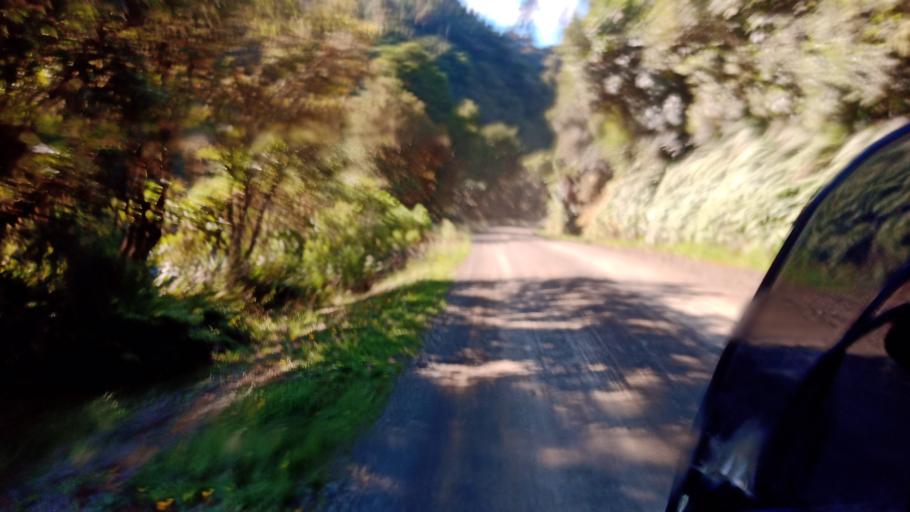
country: NZ
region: Bay of Plenty
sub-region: Opotiki District
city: Opotiki
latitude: -38.2484
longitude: 177.5909
